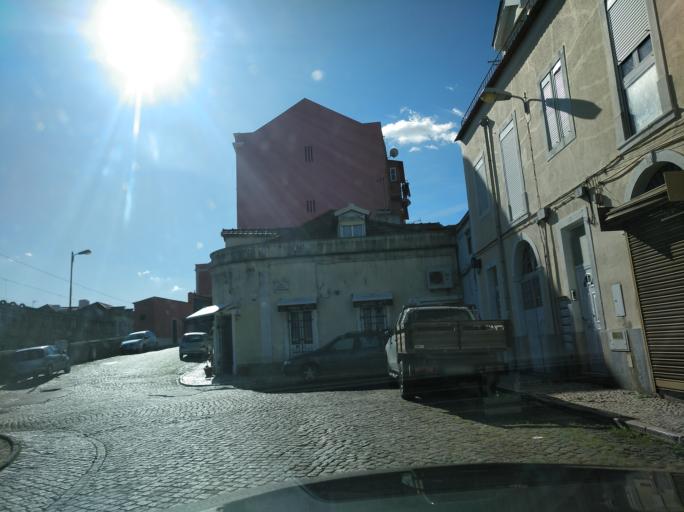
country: PT
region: Lisbon
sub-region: Loures
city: Moscavide
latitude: 38.7424
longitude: -9.1047
